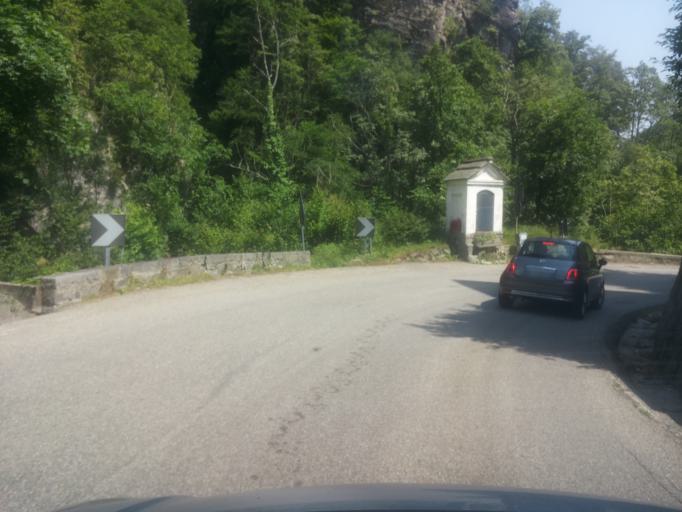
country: IT
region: Piedmont
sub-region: Provincia di Biella
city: Rosazza
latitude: 45.6750
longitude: 7.9823
